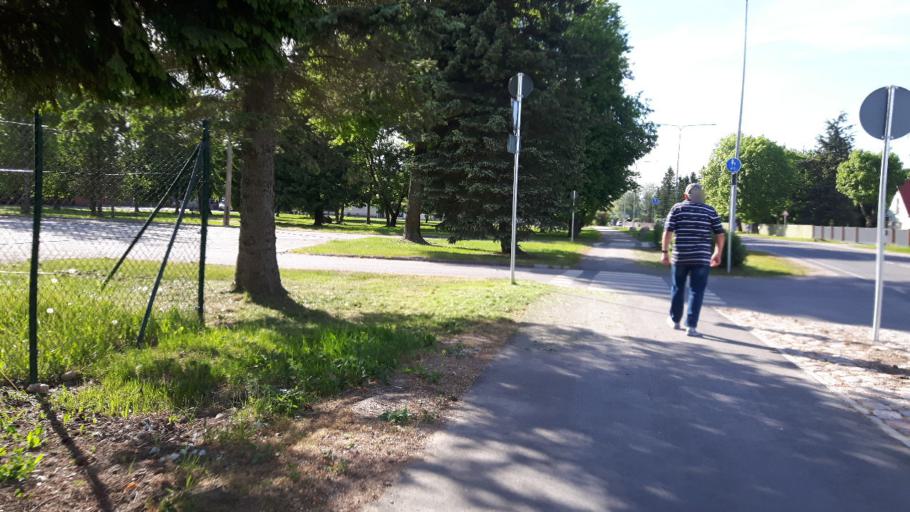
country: EE
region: Harju
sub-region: Joelaehtme vald
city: Loo
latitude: 59.4318
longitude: 24.9528
